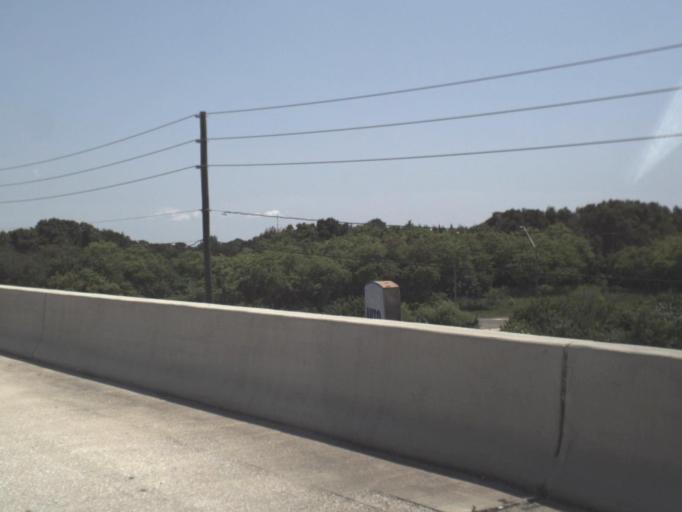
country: US
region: Florida
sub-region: Pinellas County
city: South Highpoint
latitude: 27.8800
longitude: -82.7128
